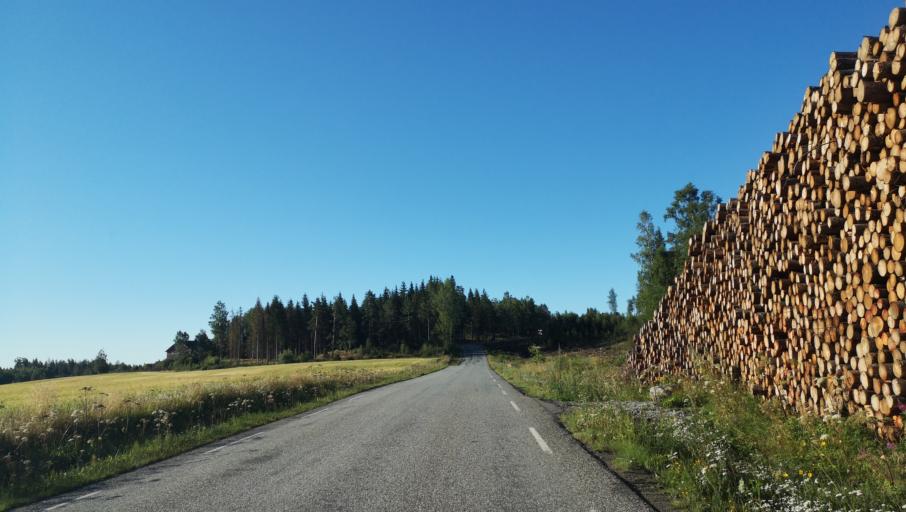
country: NO
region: Ostfold
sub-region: Hobol
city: Knappstad
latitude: 59.6364
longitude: 11.0230
